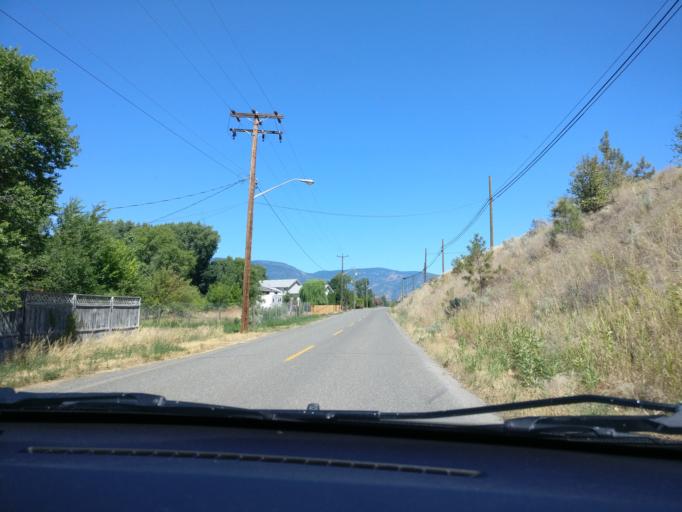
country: CA
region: British Columbia
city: Logan Lake
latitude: 50.7549
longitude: -120.8341
